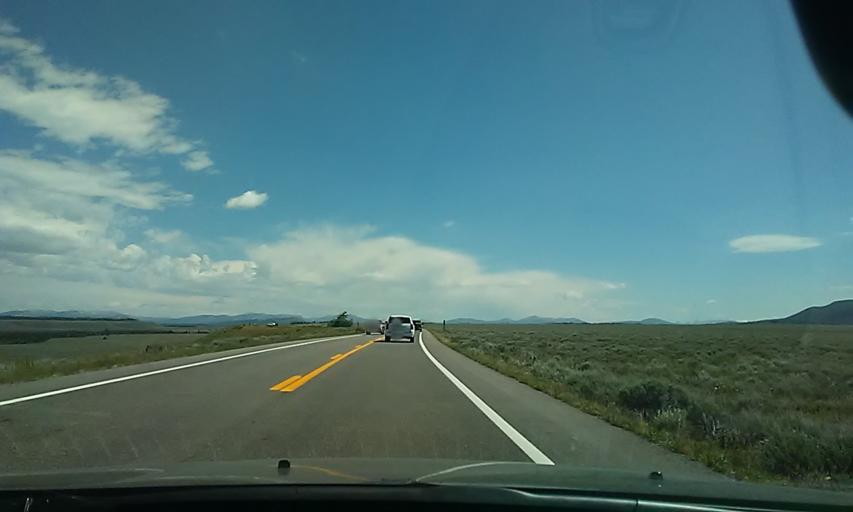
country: US
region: Wyoming
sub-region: Teton County
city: Jackson
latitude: 43.7147
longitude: -110.6626
